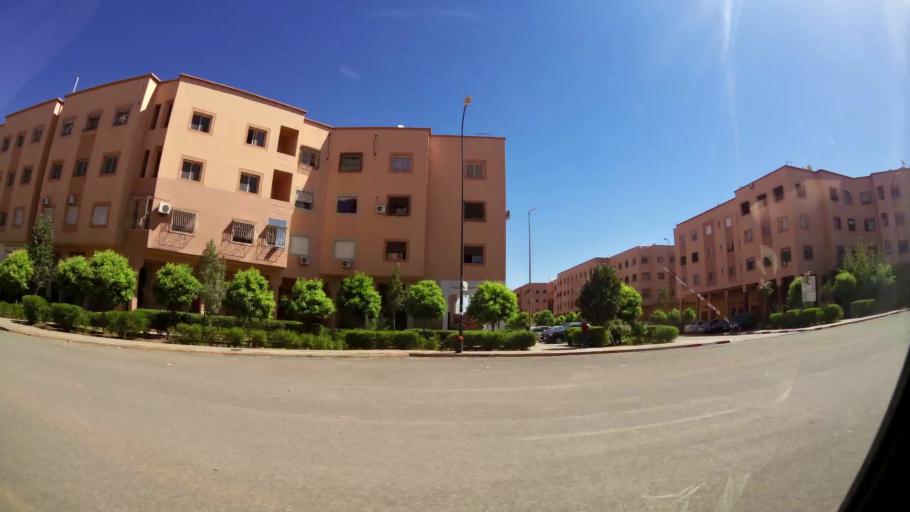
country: MA
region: Marrakech-Tensift-Al Haouz
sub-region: Marrakech
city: Marrakesh
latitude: 31.5749
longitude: -8.0581
